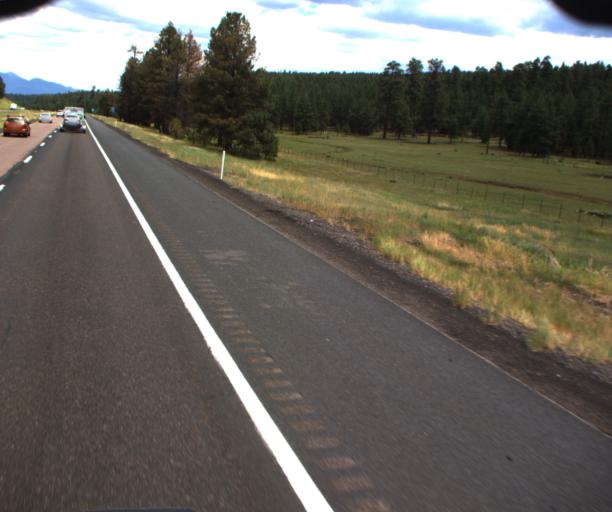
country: US
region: Arizona
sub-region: Coconino County
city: Mountainaire
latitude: 35.0268
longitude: -111.6850
